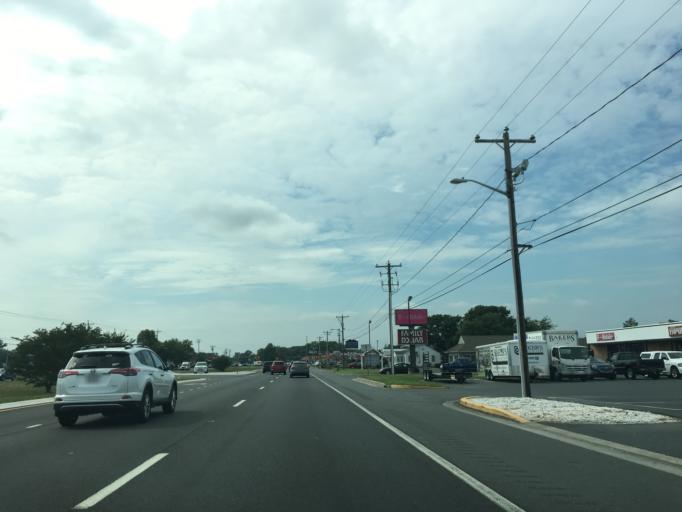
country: US
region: Delaware
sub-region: Sussex County
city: Millsboro
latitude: 38.5820
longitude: -75.2918
